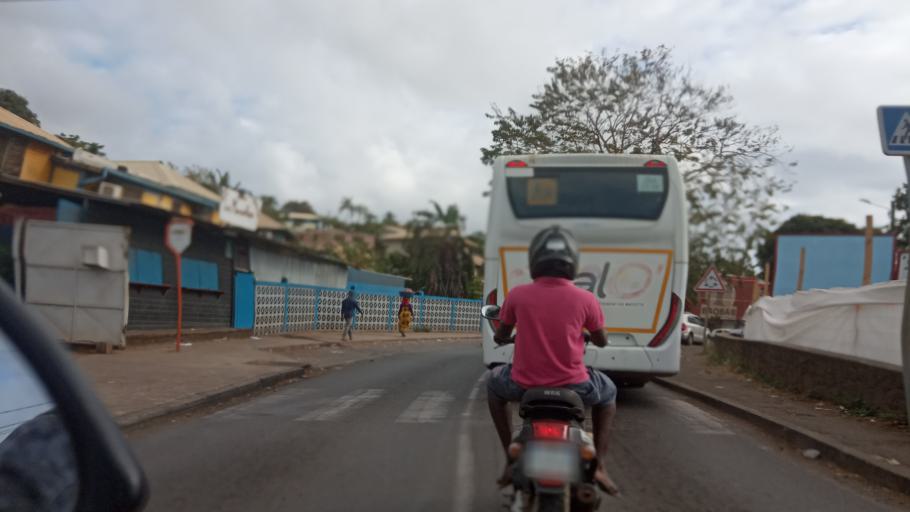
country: YT
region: Mamoudzou
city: Mamoudzou
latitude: -12.7863
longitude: 45.2255
